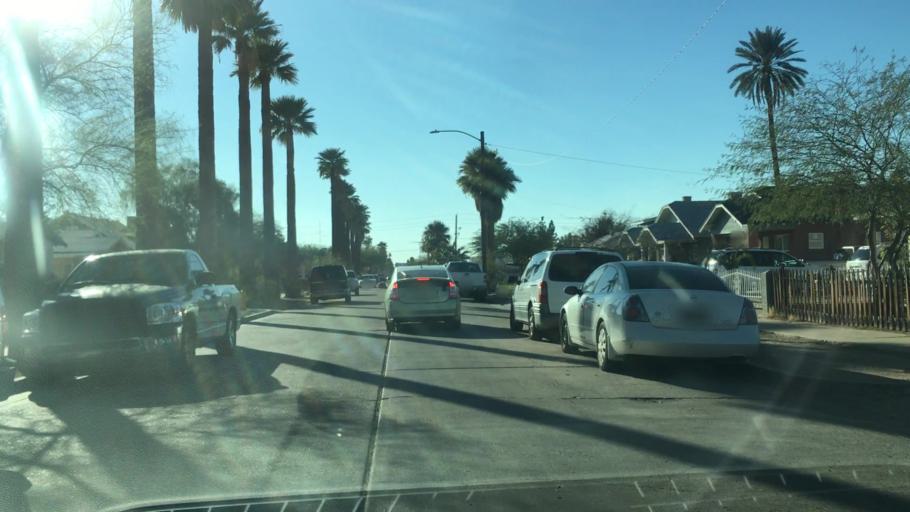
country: US
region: Arizona
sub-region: Maricopa County
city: Phoenix
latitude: 33.4568
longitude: -112.0505
